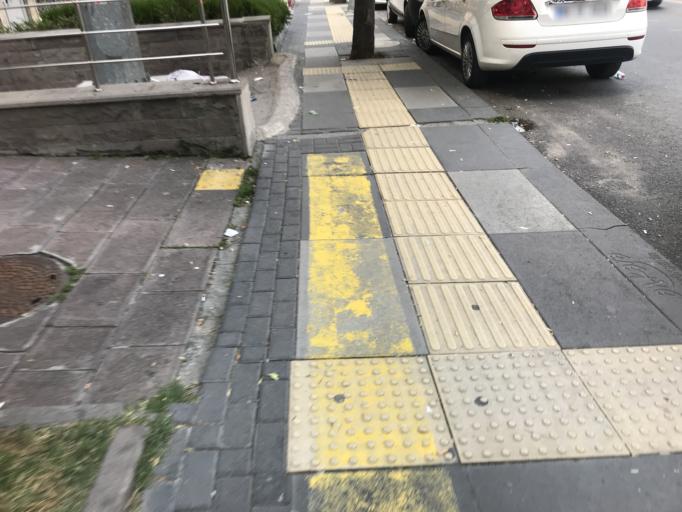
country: TR
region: Ankara
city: Ankara
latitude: 39.8757
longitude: 32.8350
